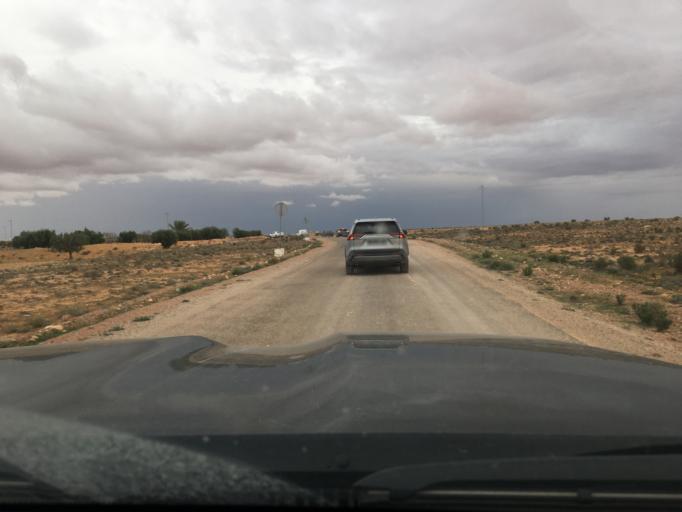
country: TN
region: Madanin
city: Medenine
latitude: 33.2874
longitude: 10.6025
